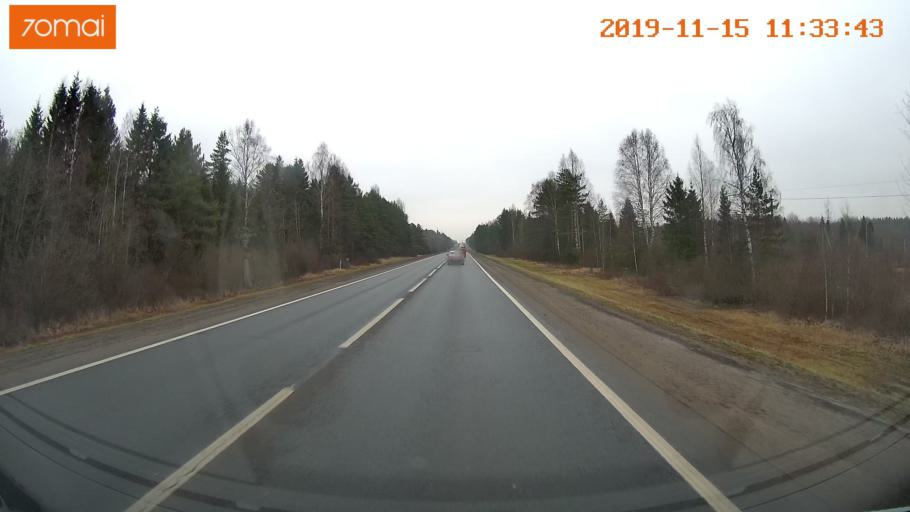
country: RU
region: Vologda
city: Molochnoye
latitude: 59.1903
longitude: 39.5970
